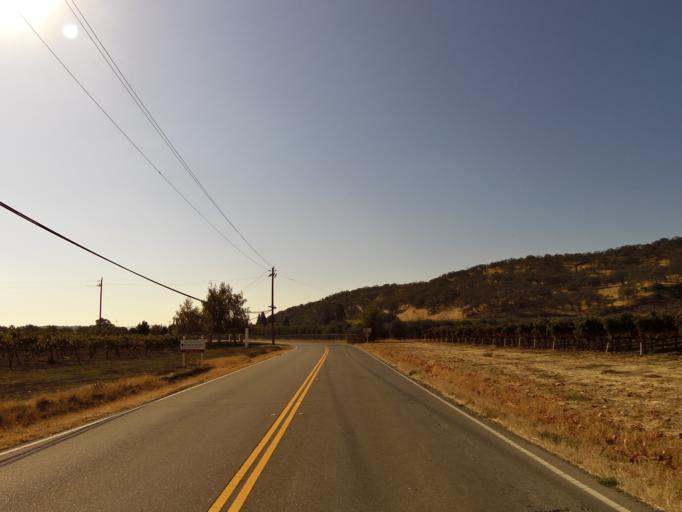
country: US
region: California
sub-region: Solano County
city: Green Valley
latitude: 38.2548
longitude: -122.1195
